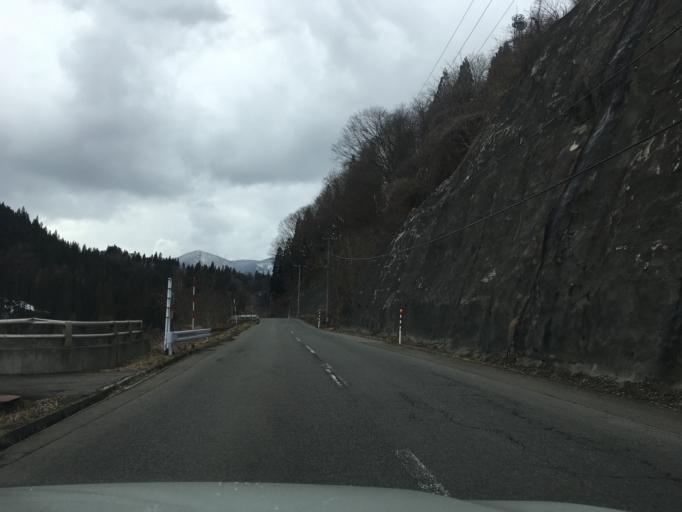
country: JP
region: Akita
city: Odate
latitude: 40.4278
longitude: 140.6498
